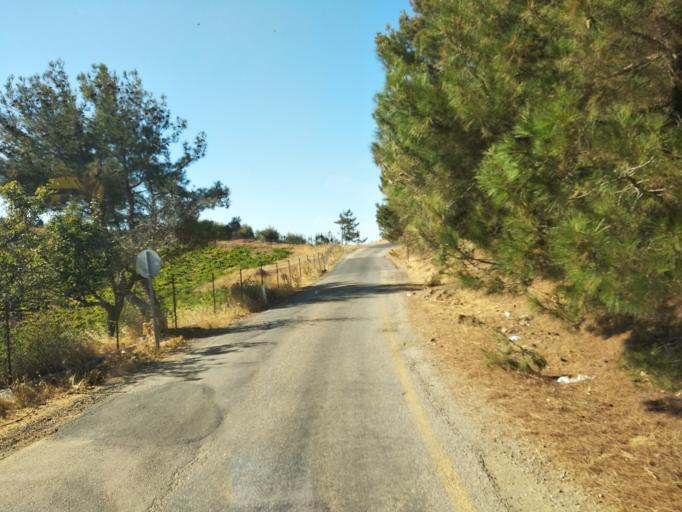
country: TR
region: Izmir
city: Gaziemir
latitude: 38.3063
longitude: 26.9988
